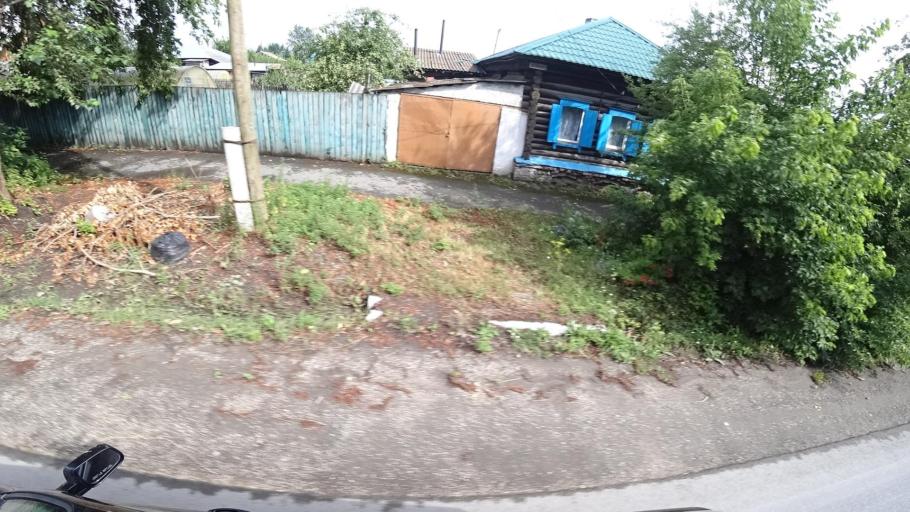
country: RU
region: Sverdlovsk
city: Kamyshlov
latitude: 56.8406
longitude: 62.7182
